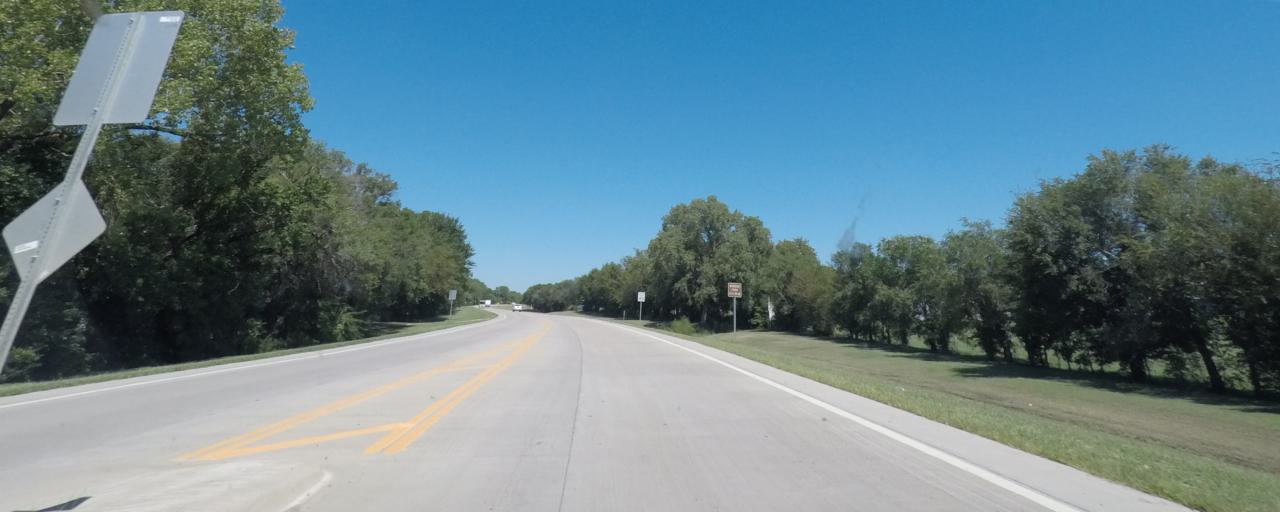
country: US
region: Kansas
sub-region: Sumner County
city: Wellington
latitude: 37.2541
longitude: -97.4040
